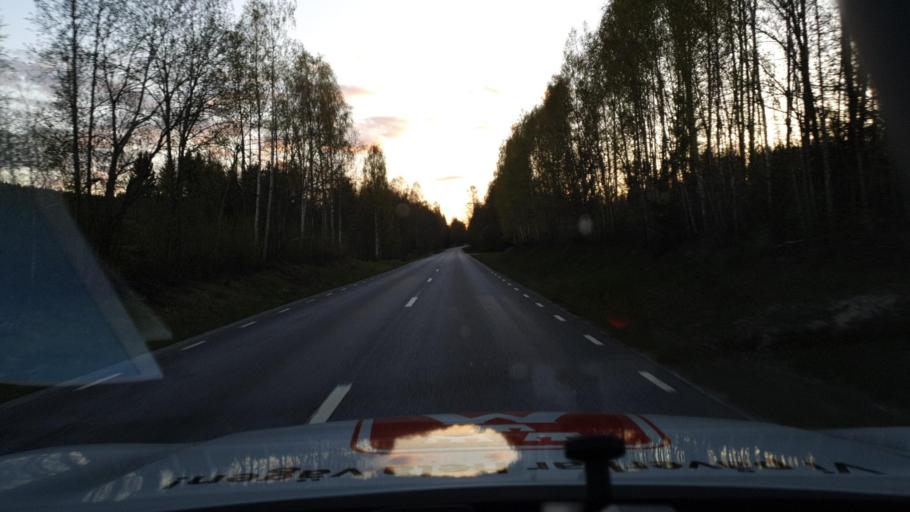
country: SE
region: Vaestmanland
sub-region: Skinnskattebergs Kommun
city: Skinnskatteberg
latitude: 59.8951
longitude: 15.5845
